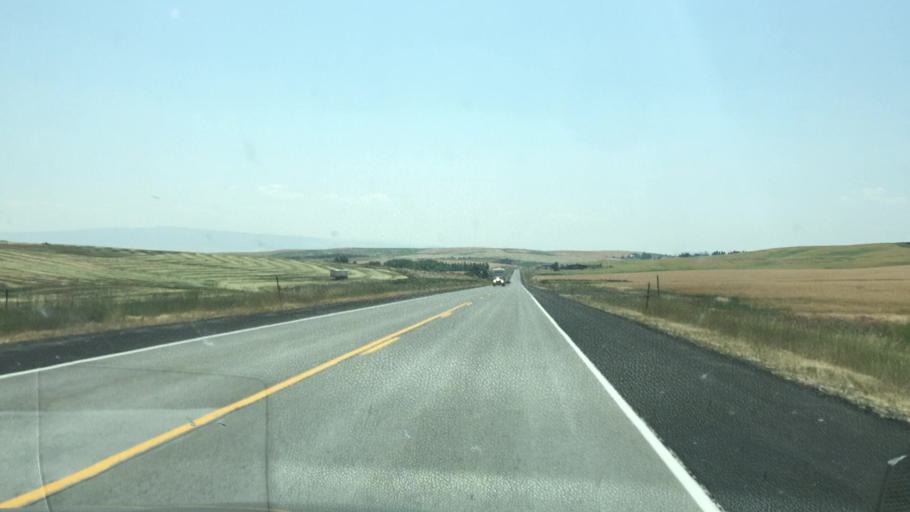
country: US
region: Idaho
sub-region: Lewis County
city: Nezperce
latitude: 46.0891
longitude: -116.3471
